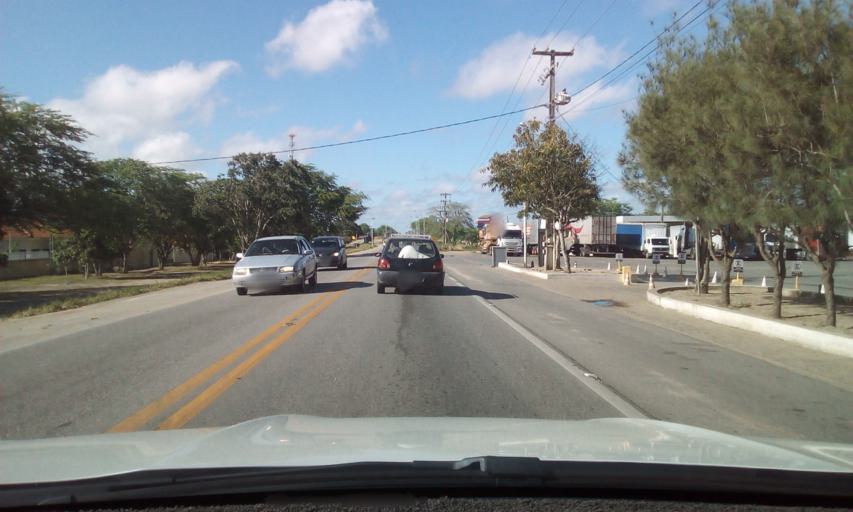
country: BR
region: Paraiba
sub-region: Campina Grande
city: Campina Grande
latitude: -7.2879
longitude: -35.8899
